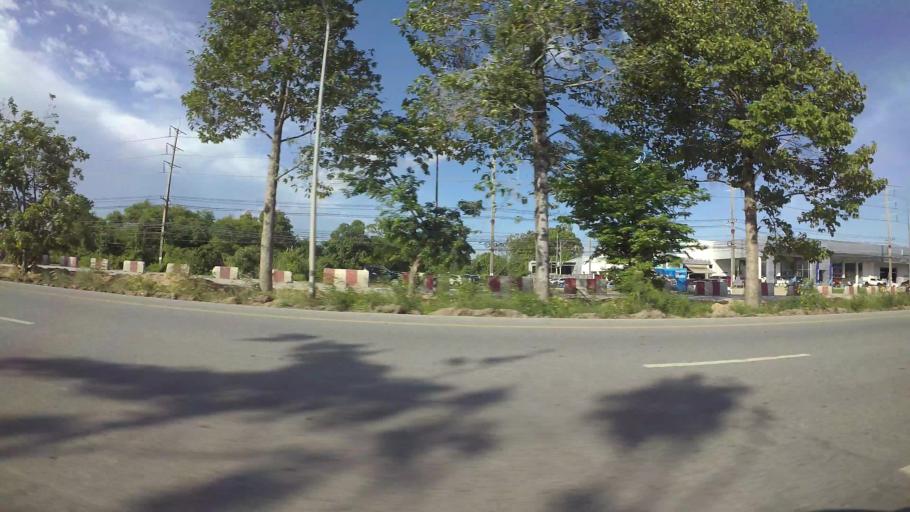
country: TH
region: Rayong
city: Rayong
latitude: 12.6702
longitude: 101.3059
